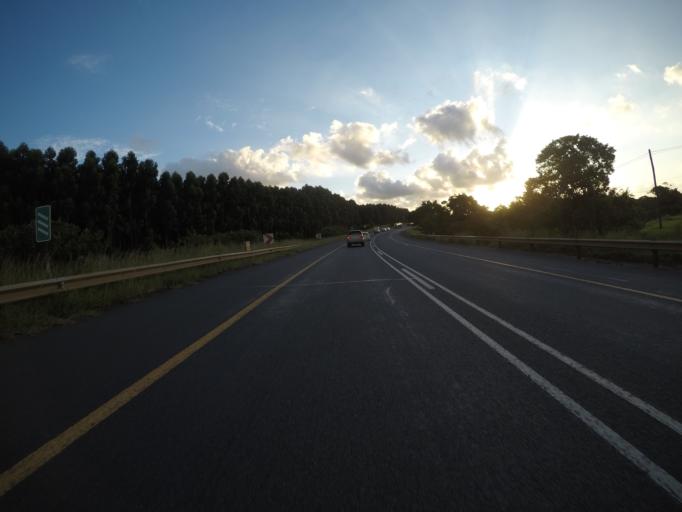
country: ZA
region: KwaZulu-Natal
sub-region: uThungulu District Municipality
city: Richards Bay
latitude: -28.6921
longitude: 32.0361
